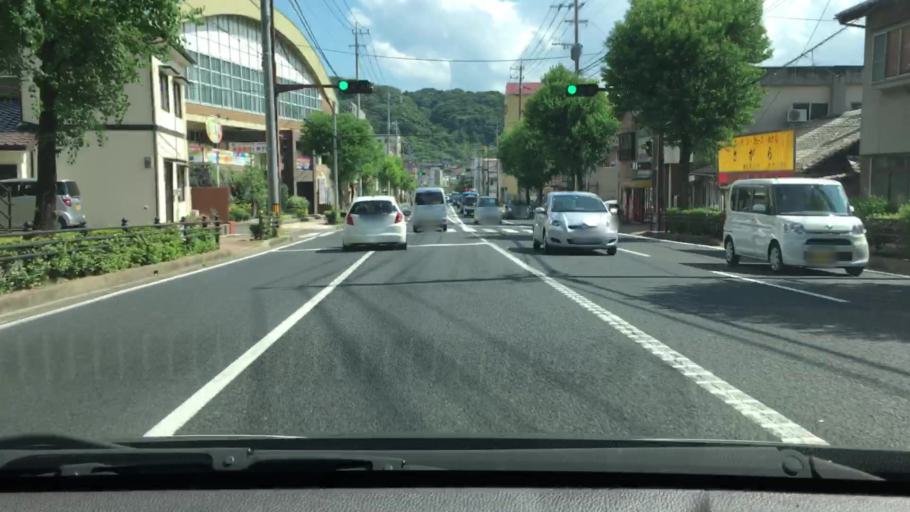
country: JP
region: Nagasaki
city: Sasebo
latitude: 33.2011
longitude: 129.7211
